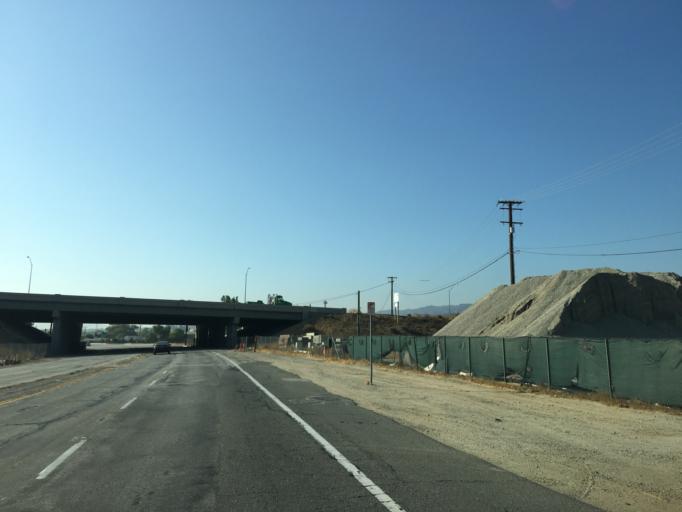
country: US
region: California
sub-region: Los Angeles County
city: Valencia
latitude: 34.4427
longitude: -118.6086
